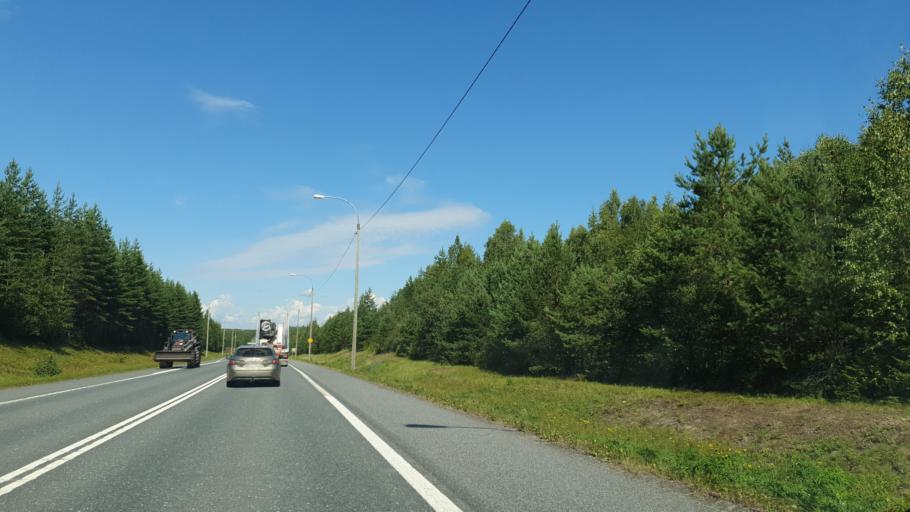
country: FI
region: Northern Savo
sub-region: Ylae-Savo
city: Iisalmi
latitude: 63.5844
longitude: 27.2310
